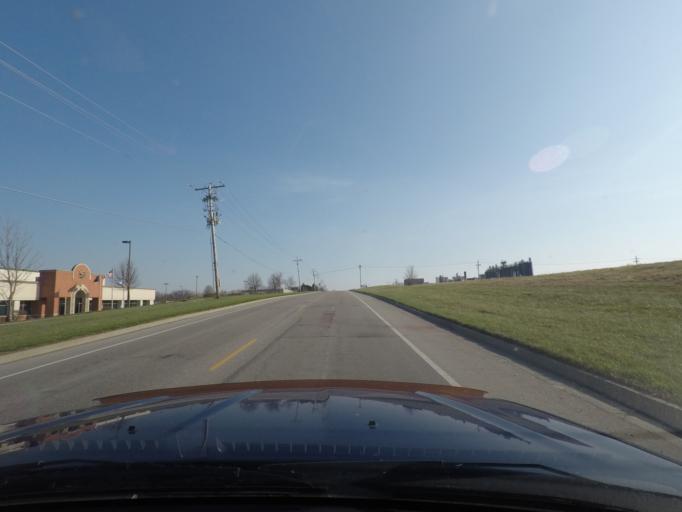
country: US
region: Kansas
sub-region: Douglas County
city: Lawrence
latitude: 38.9996
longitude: -95.2605
